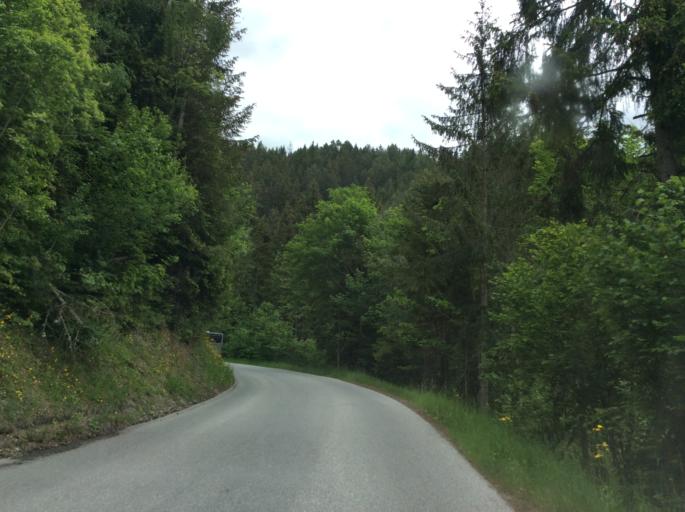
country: AT
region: Styria
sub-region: Politischer Bezirk Liezen
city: Schladming
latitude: 47.4058
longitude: 13.6943
